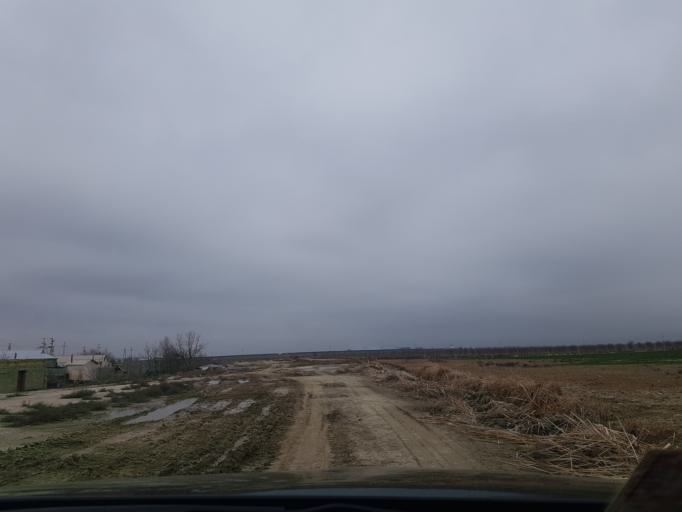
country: TM
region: Ahal
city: Abadan
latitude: 38.1417
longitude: 57.9673
